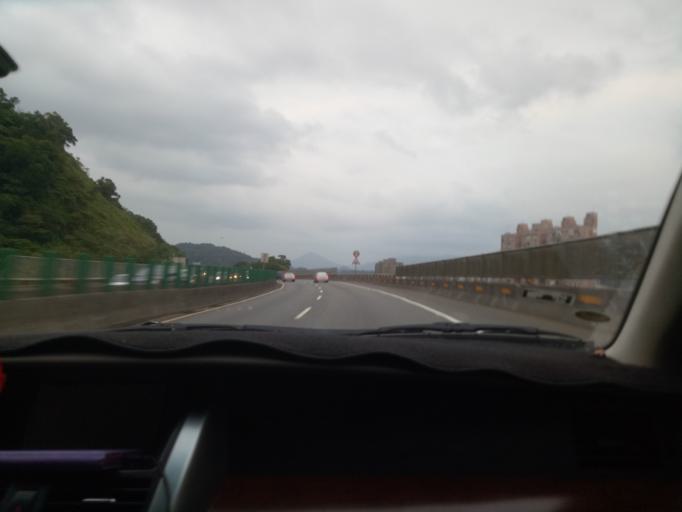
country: TW
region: Taiwan
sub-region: Keelung
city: Keelung
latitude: 25.1007
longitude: 121.7502
